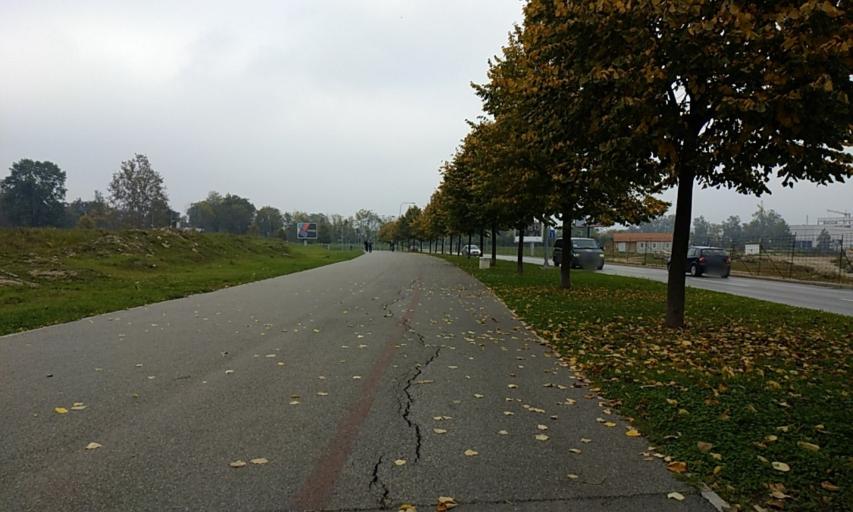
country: BA
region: Republika Srpska
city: Banja Luka
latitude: 44.7772
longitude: 17.2021
